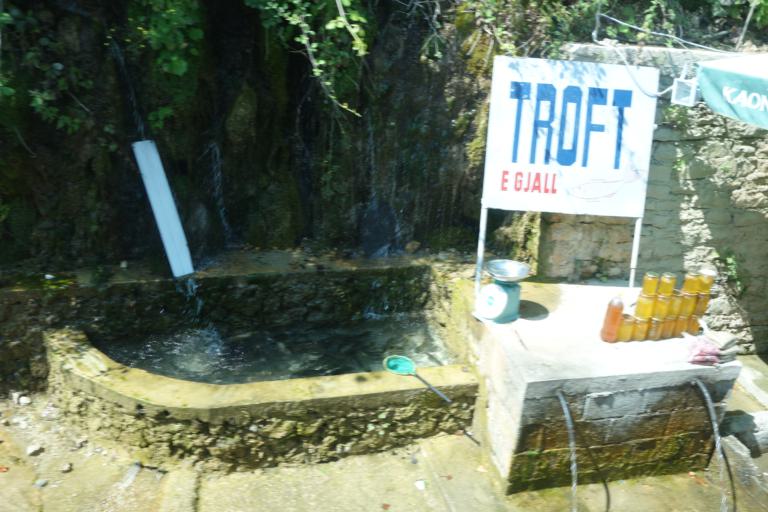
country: AL
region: Gjirokaster
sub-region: Rrethi i Tepelenes
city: Tepelene
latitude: 40.2570
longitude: 20.0563
